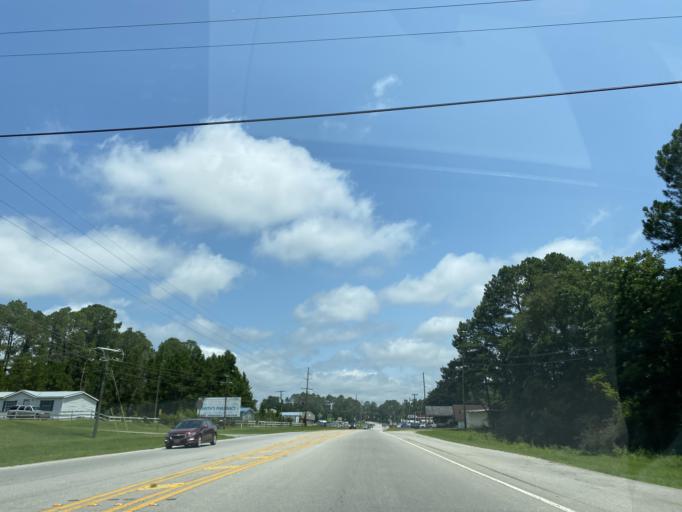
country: US
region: Georgia
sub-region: Telfair County
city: McRae
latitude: 32.0552
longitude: -82.9065
